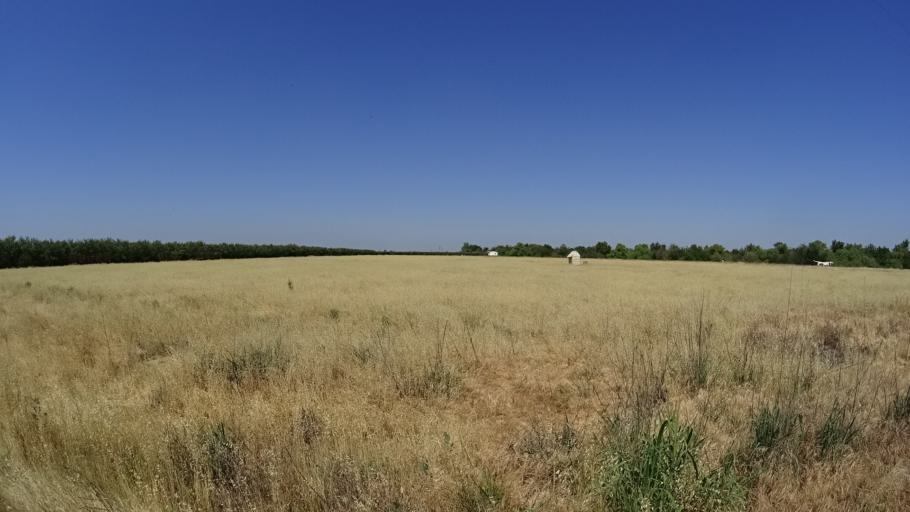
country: US
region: California
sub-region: Fresno County
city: Kingsburg
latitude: 36.4575
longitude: -119.5913
